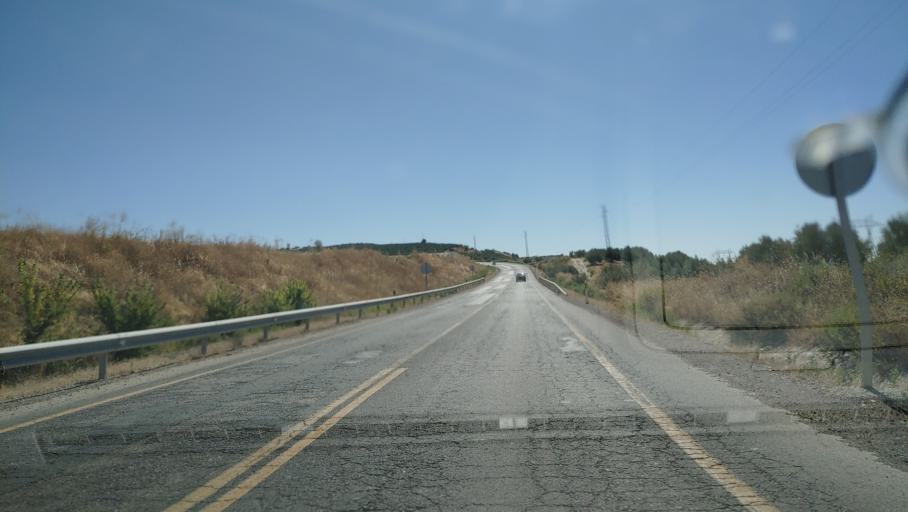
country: ES
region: Andalusia
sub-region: Provincia de Jaen
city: Iznatoraf
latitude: 38.1387
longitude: -3.0469
